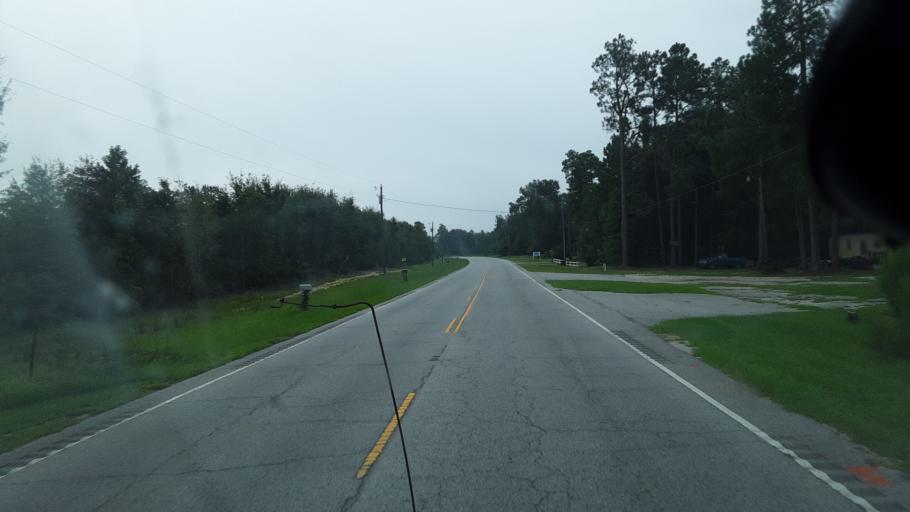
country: US
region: South Carolina
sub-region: Florence County
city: Johnsonville
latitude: 33.8986
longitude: -79.3929
